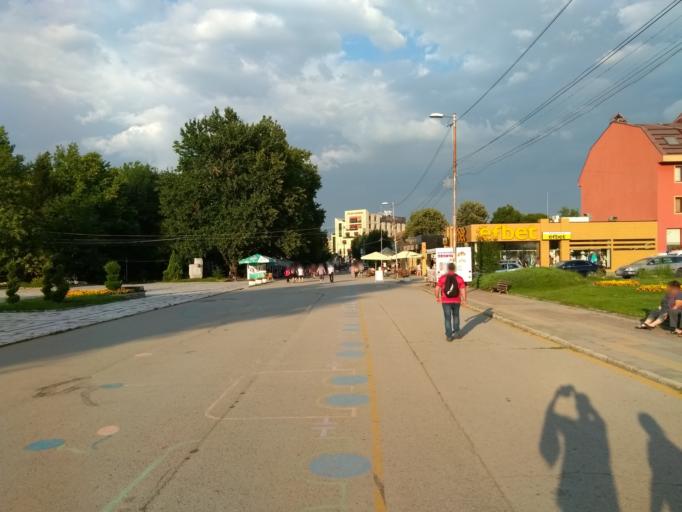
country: BG
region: Stara Zagora
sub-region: Obshtina Pavel Banya
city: Pavel Banya
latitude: 42.5974
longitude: 25.2083
